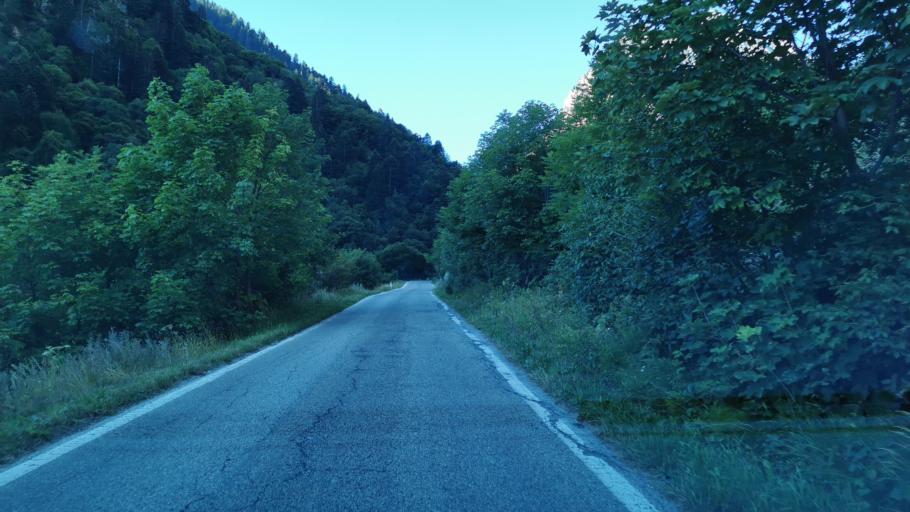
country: IT
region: Piedmont
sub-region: Provincia di Cuneo
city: Demonte
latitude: 44.2138
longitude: 7.2784
